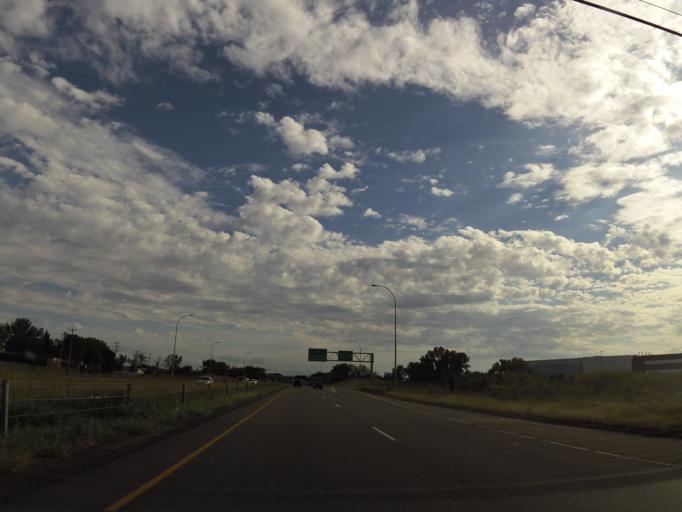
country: US
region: Minnesota
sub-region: Hennepin County
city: New Hope
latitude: 45.0477
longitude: -93.4010
